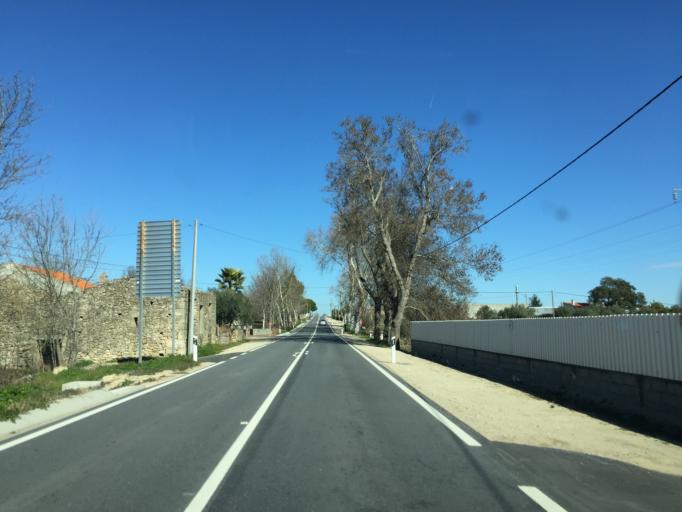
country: PT
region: Guarda
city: Alcains
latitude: 39.9252
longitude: -7.4659
